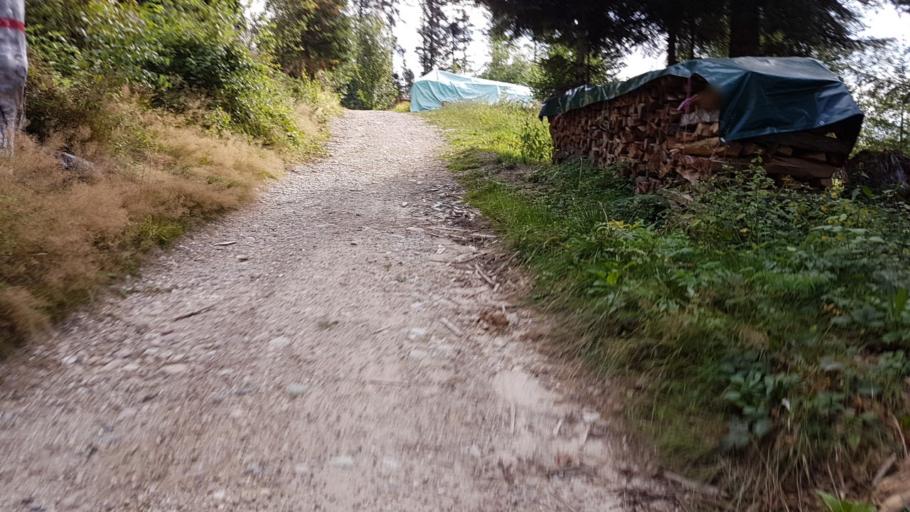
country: CH
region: Bern
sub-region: Bern-Mittelland District
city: Linden
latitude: 46.8547
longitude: 7.6546
